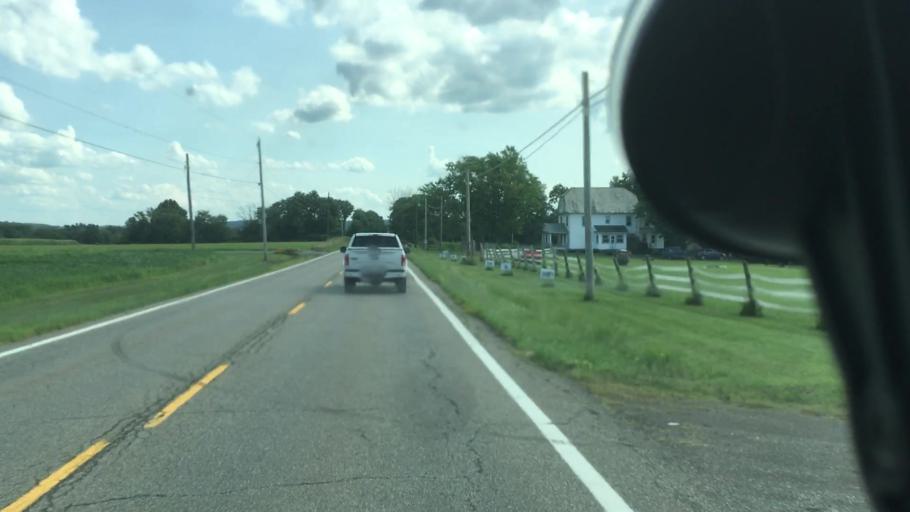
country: US
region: Ohio
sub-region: Columbiana County
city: Salem
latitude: 40.9667
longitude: -80.8295
